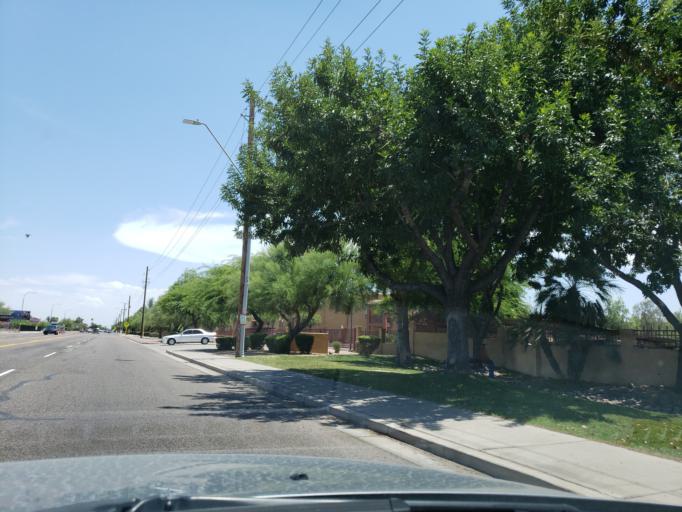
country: US
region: Arizona
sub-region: Maricopa County
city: Tolleson
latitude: 33.4653
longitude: -112.2098
